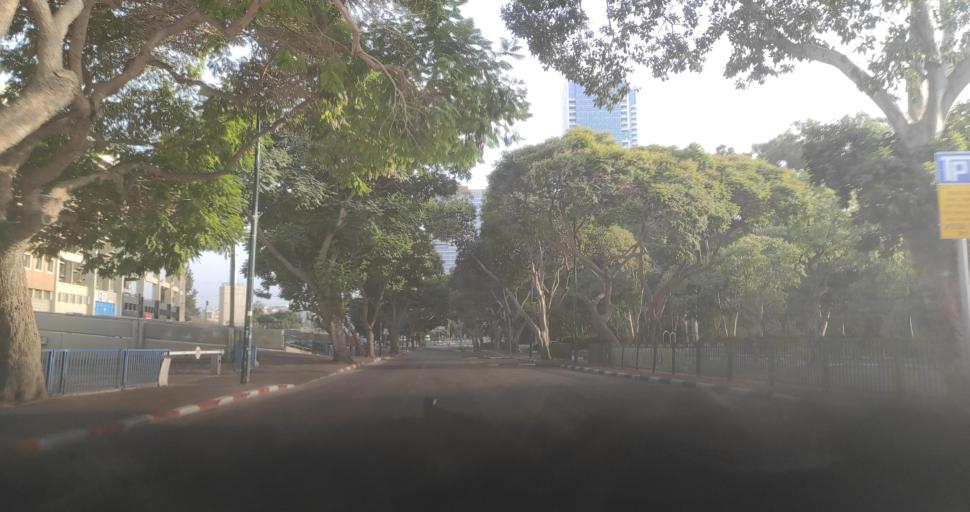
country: IL
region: Tel Aviv
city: Ramat Gan
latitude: 32.1007
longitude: 34.8228
